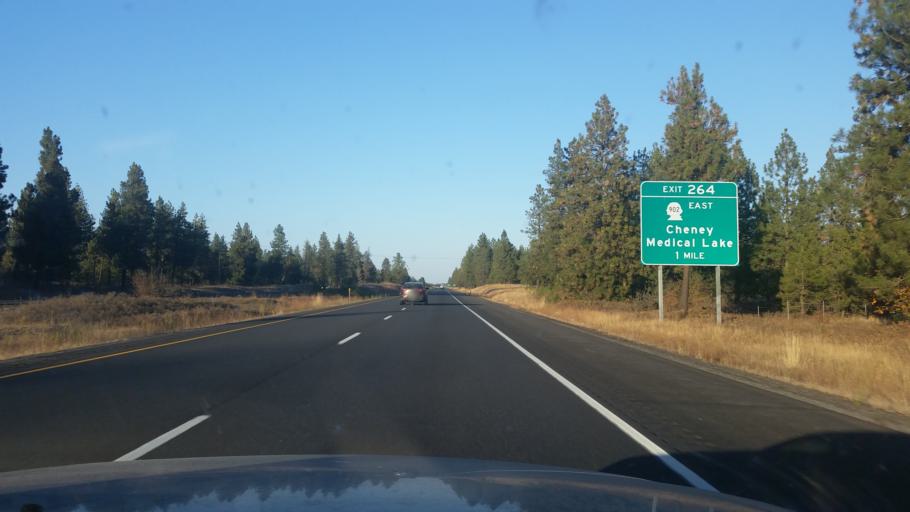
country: US
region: Washington
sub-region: Spokane County
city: Medical Lake
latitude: 47.4914
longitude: -117.7096
